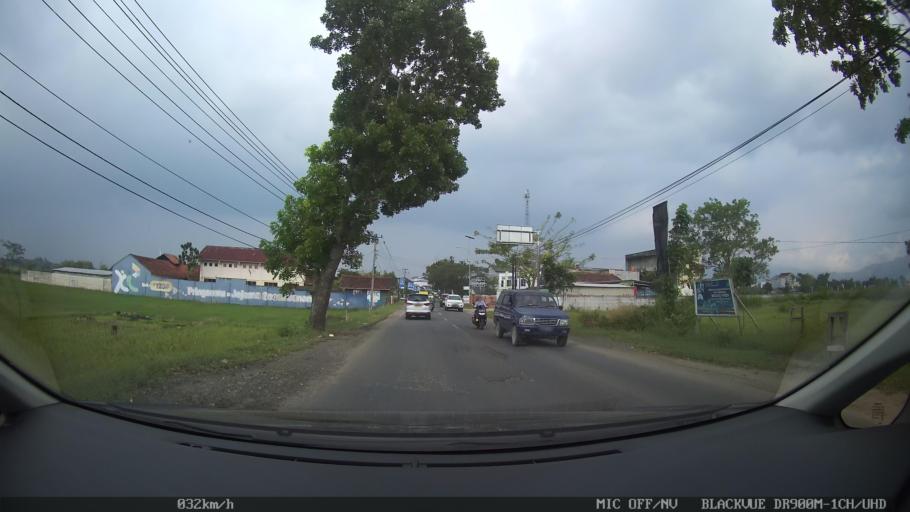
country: ID
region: Lampung
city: Gadingrejo
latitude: -5.3703
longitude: 105.0522
